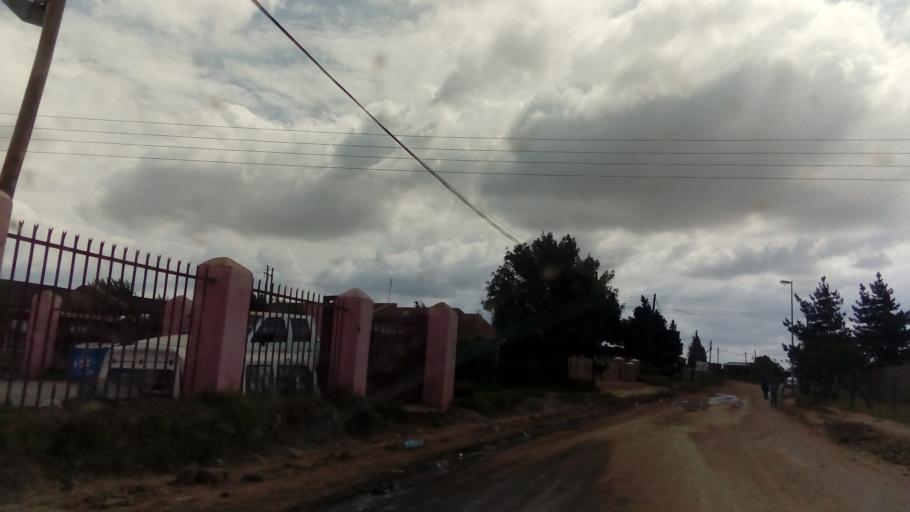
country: LS
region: Maseru
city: Maseru
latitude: -29.3709
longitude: 27.5334
